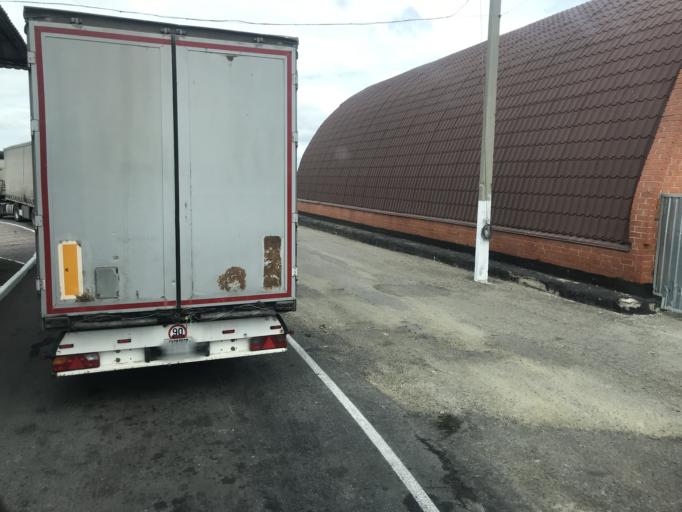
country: RU
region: Chelyabinsk
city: Troitsk
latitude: 54.0010
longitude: 61.6396
